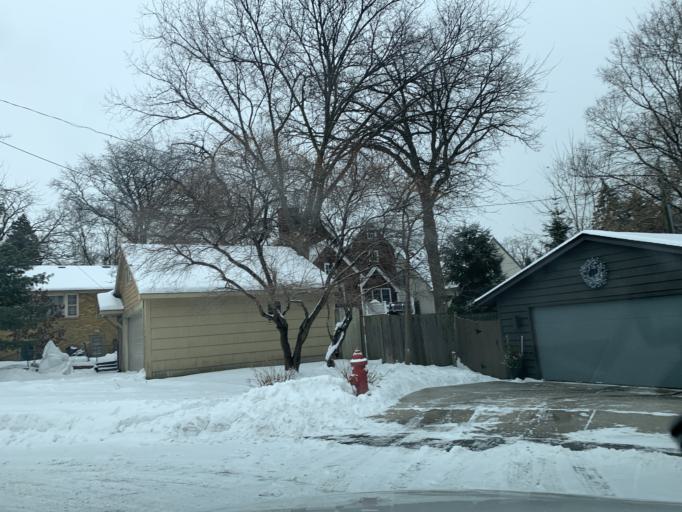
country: US
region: Minnesota
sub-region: Hennepin County
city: Saint Louis Park
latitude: 44.9428
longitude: -93.3323
